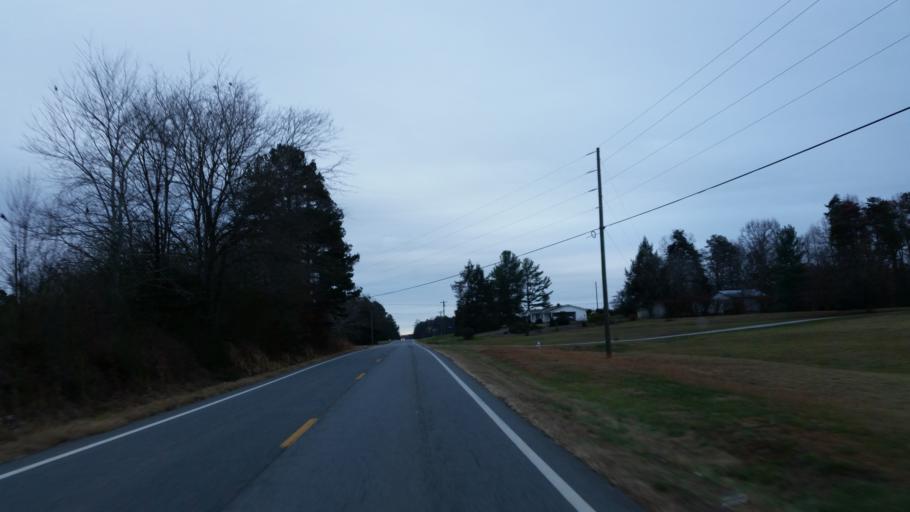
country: US
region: Georgia
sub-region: Dawson County
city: Dawsonville
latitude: 34.4611
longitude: -84.1436
